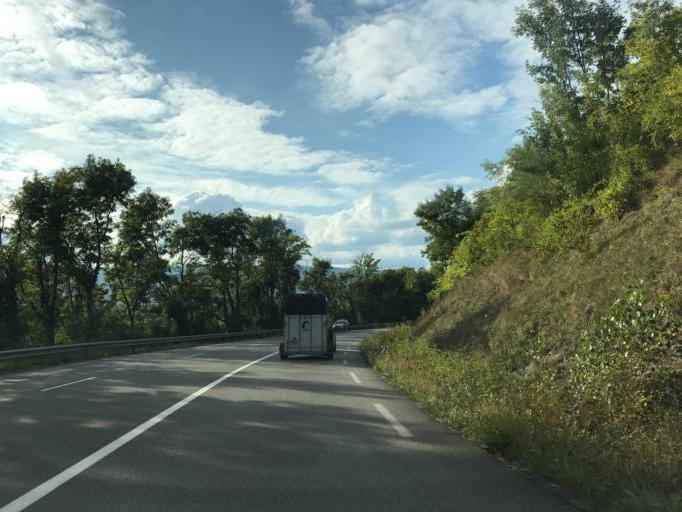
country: FR
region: Rhone-Alpes
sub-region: Departement de l'Ain
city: Bellegarde-sur-Valserine
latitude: 46.0924
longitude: 5.8566
